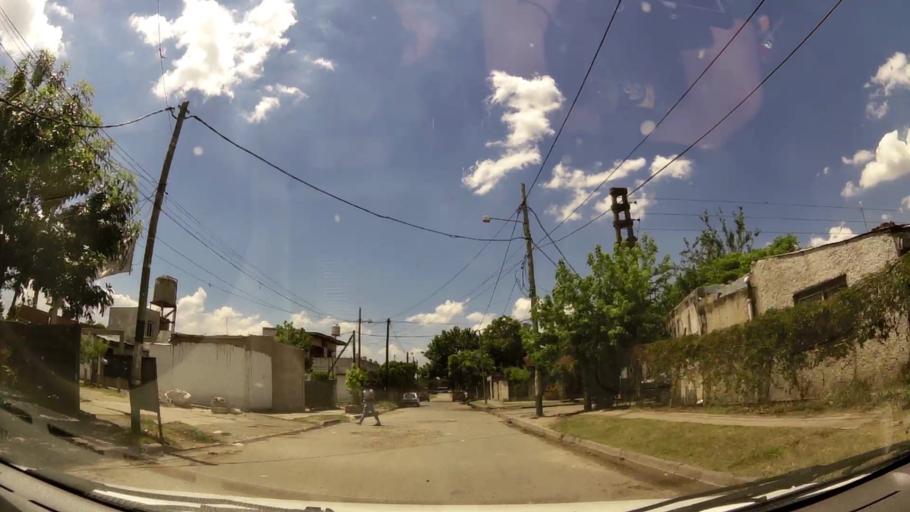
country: AR
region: Buenos Aires
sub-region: Partido de Merlo
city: Merlo
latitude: -34.6448
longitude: -58.6952
